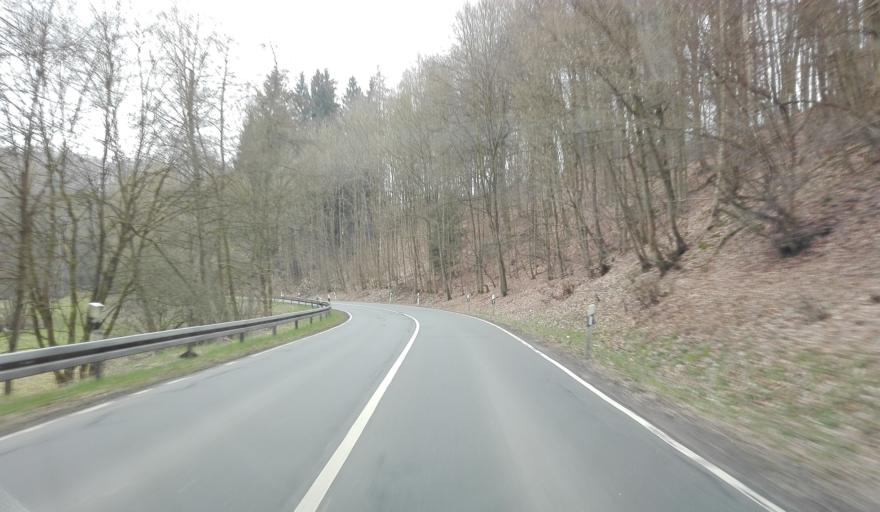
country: DE
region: Hesse
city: Lutzelbach
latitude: 49.7597
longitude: 8.7252
